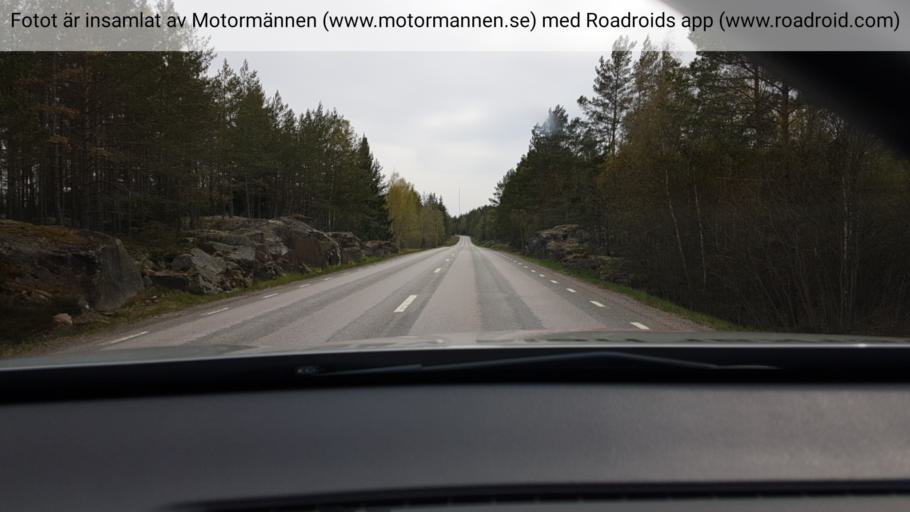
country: SE
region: Stockholm
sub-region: Norrtalje Kommun
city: Nykvarn
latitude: 59.8930
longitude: 18.0853
